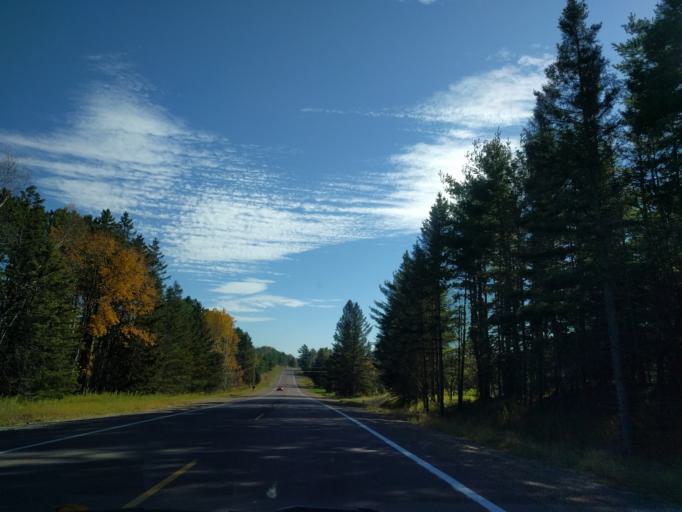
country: US
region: Michigan
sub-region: Marquette County
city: West Ishpeming
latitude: 46.3511
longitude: -87.9800
